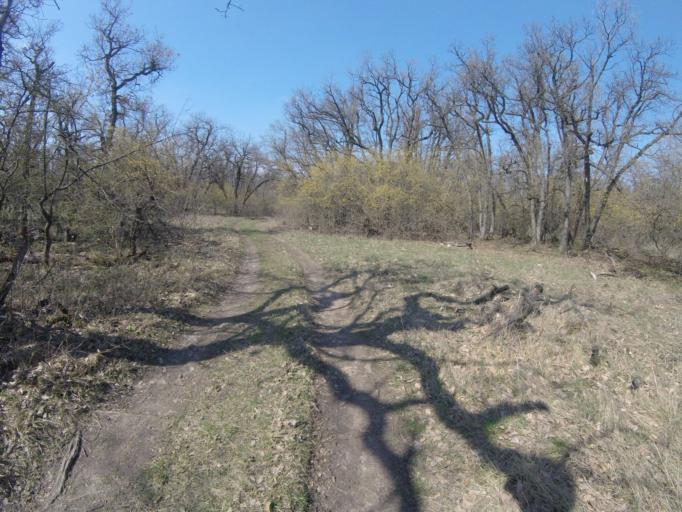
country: HU
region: Pest
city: Budakeszi
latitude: 47.5385
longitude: 18.8911
